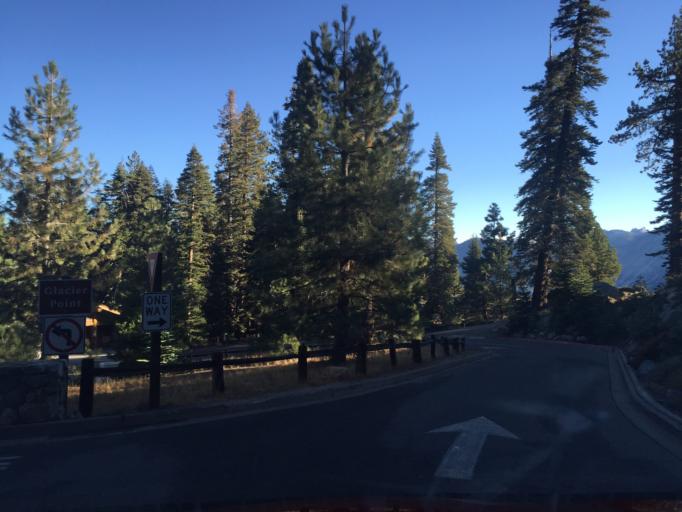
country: US
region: California
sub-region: Mariposa County
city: Yosemite Valley
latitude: 37.7272
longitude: -119.5745
